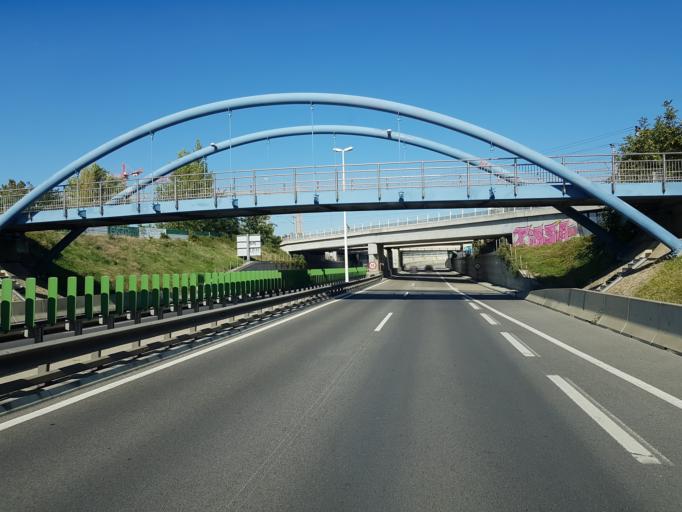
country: AT
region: Lower Austria
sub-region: Politischer Bezirk Korneuburg
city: Langenzersdorf
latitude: 48.2708
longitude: 16.3986
